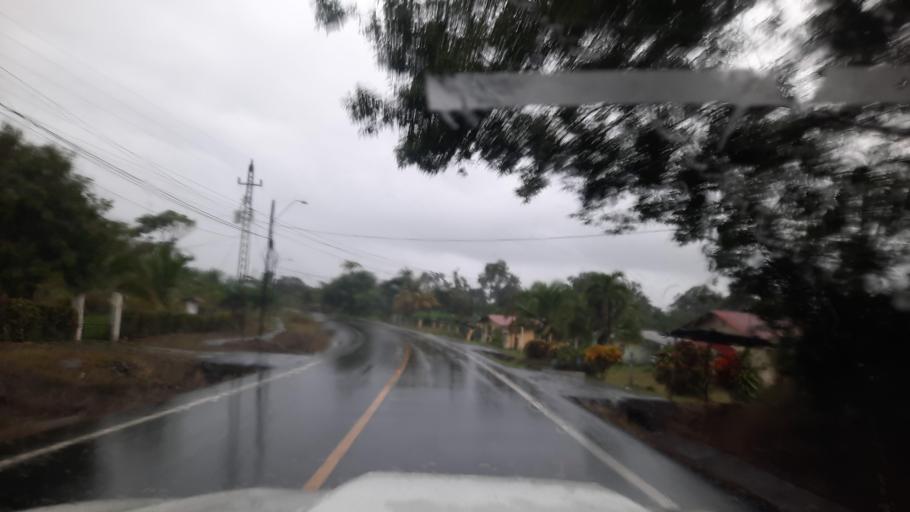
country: PA
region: Chiriqui
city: Sortova
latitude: 8.5795
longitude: -82.6373
